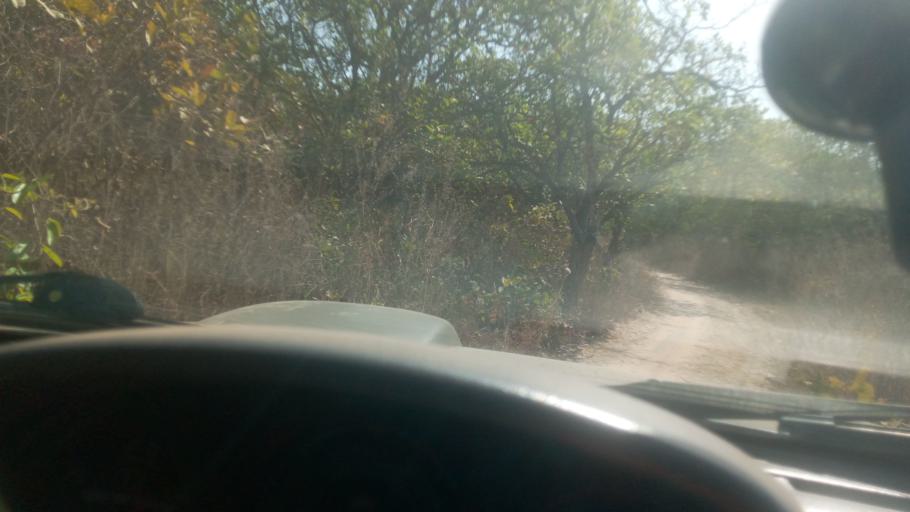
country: GW
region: Oio
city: Farim
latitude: 12.4494
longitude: -15.4276
